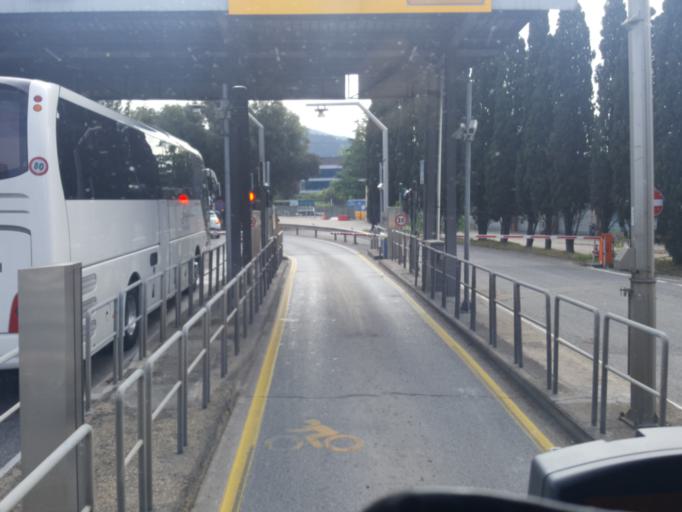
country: IT
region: Tuscany
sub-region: Province of Florence
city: Calenzano
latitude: 43.8519
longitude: 11.1686
